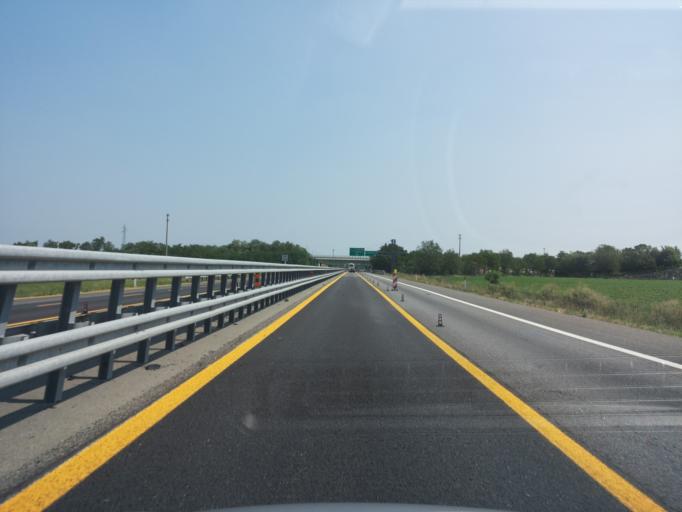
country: IT
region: Lombardy
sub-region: Provincia di Pavia
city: Casei
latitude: 44.9964
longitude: 8.9663
